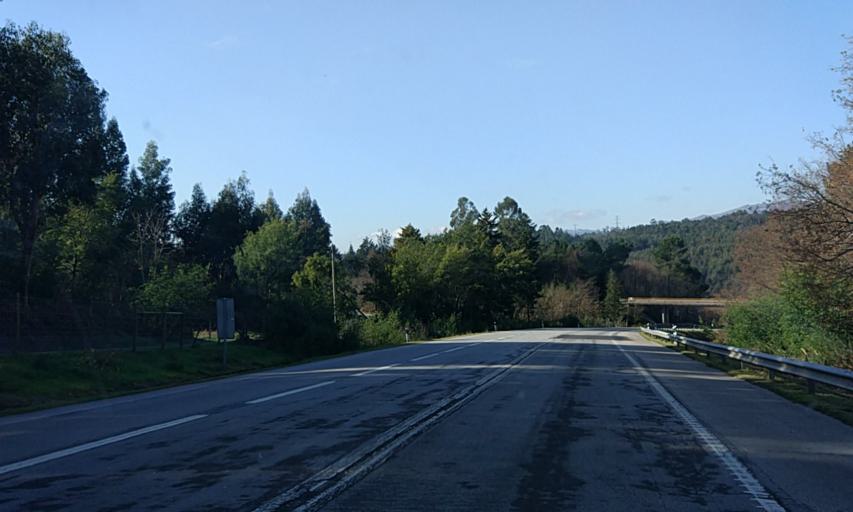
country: PT
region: Viseu
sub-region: Viseu
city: Abraveses
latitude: 40.6731
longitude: -7.9864
